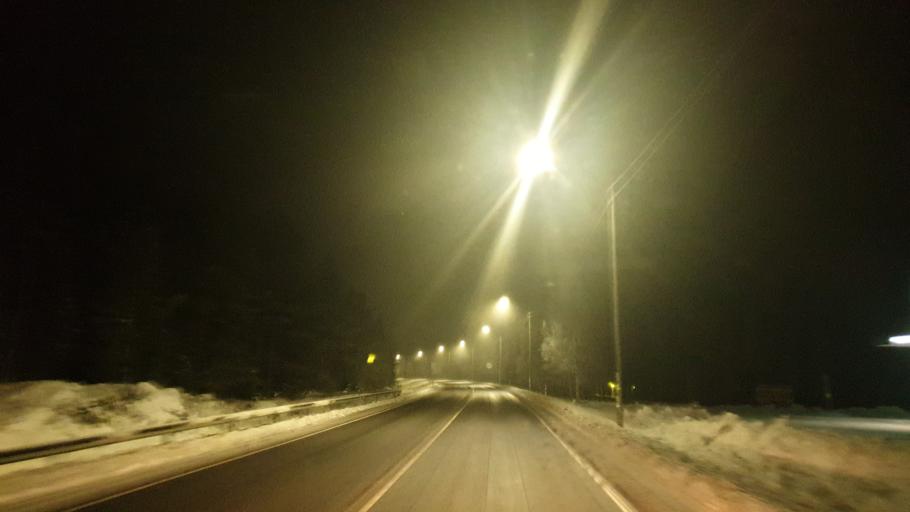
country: FI
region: Northern Ostrobothnia
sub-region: Oulunkaari
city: Kuivaniemi
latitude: 65.5264
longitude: 25.2595
